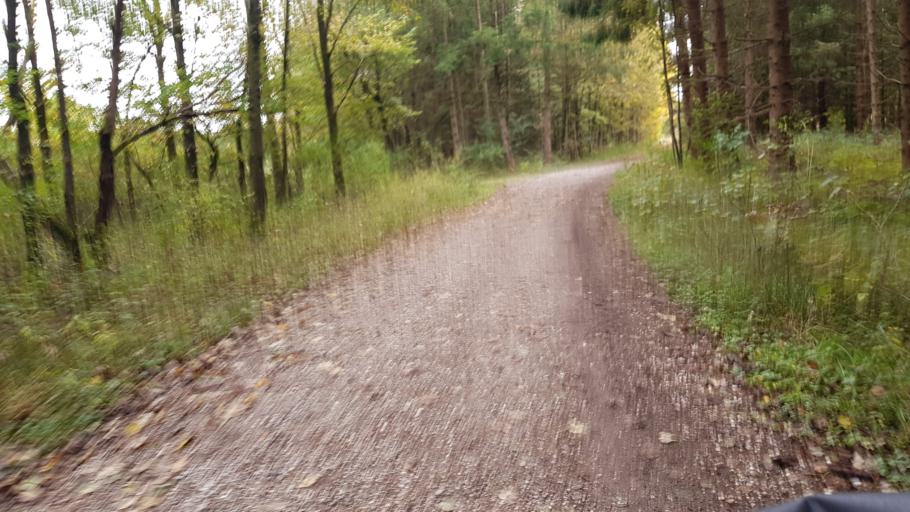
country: DE
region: Bavaria
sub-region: Upper Bavaria
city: Germering
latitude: 48.1060
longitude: 11.3479
